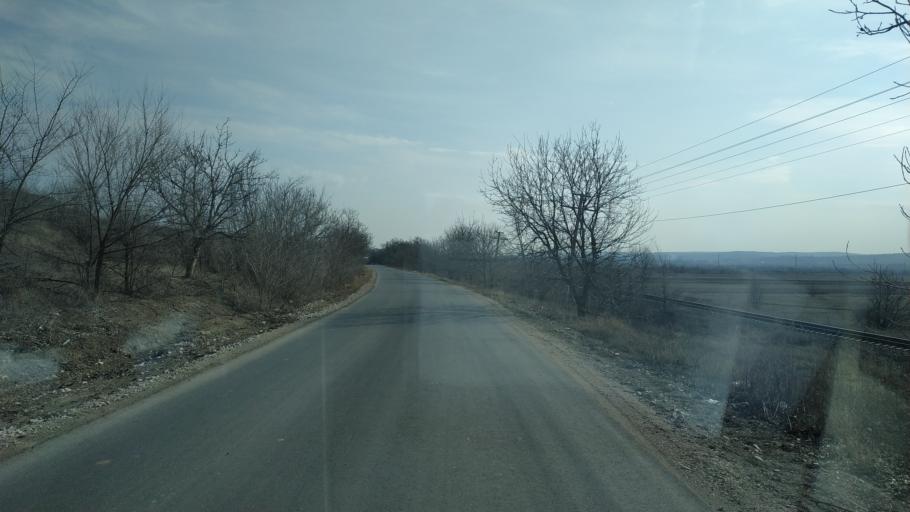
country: MD
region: Chisinau
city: Singera
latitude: 46.9193
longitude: 29.0994
